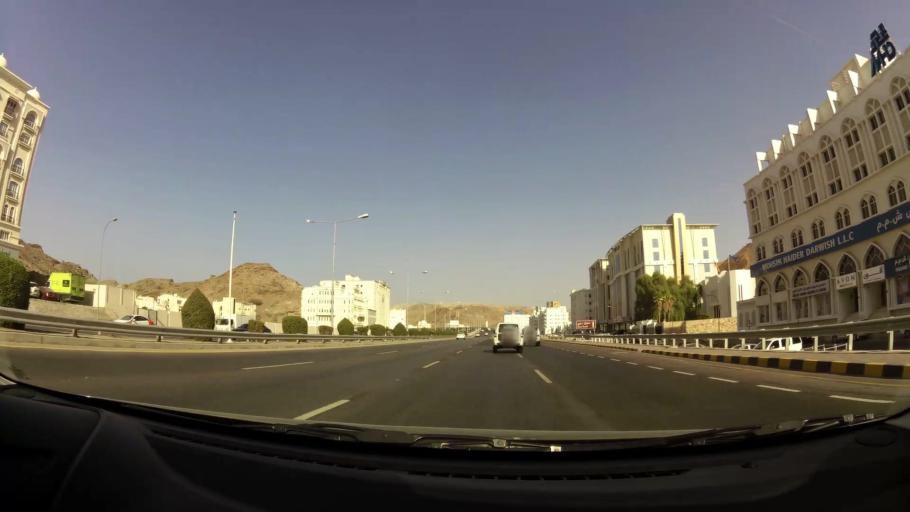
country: OM
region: Muhafazat Masqat
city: Muscat
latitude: 23.5881
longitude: 58.5345
